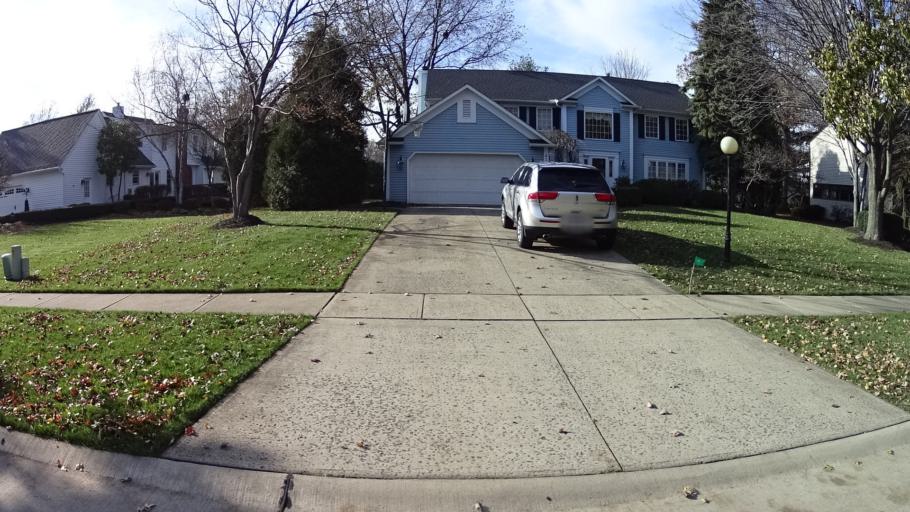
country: US
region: Ohio
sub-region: Lorain County
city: Avon Lake
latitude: 41.4984
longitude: -81.9809
